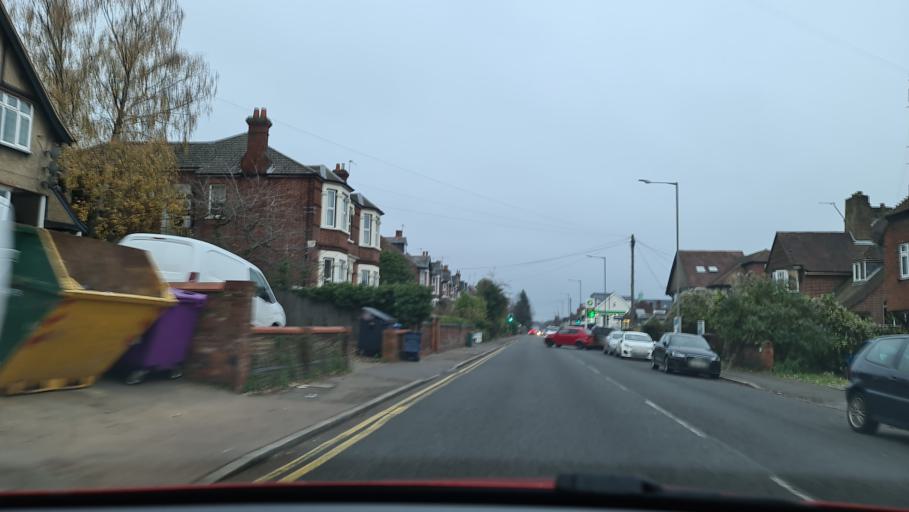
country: GB
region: England
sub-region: Buckinghamshire
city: High Wycombe
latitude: 51.6367
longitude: -0.7701
